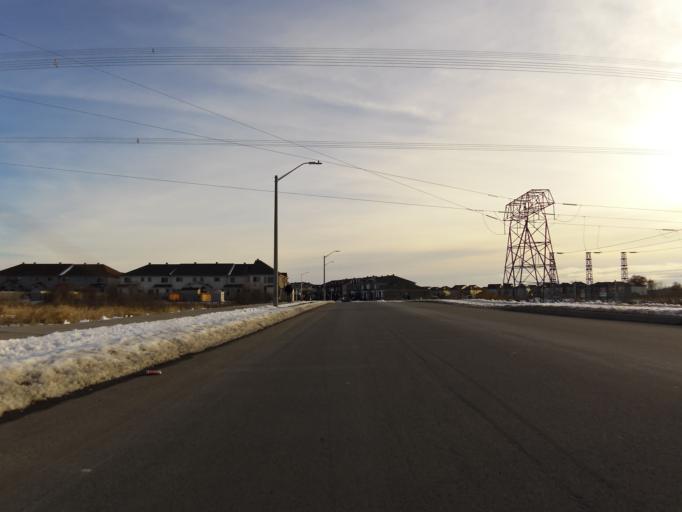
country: CA
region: Ontario
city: Bells Corners
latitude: 45.2837
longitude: -75.8735
